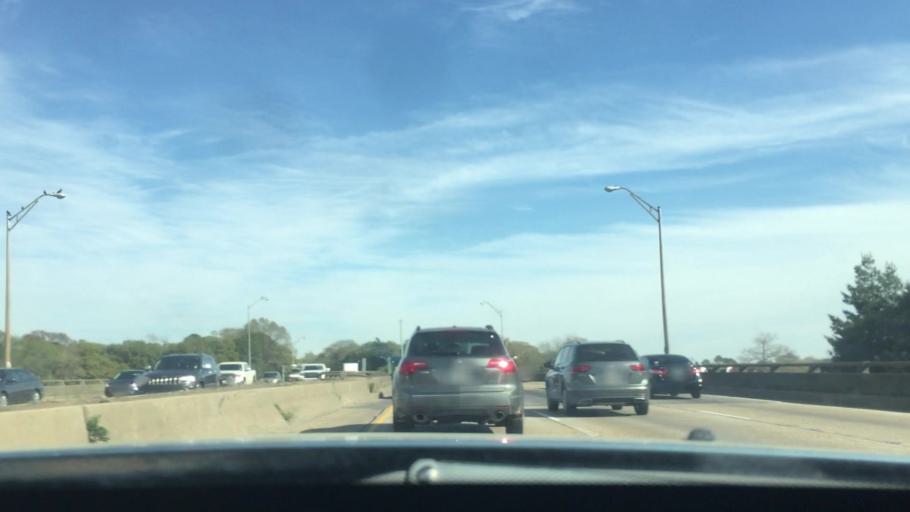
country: US
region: Louisiana
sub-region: East Baton Rouge Parish
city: Baton Rouge
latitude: 30.4273
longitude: -91.1691
